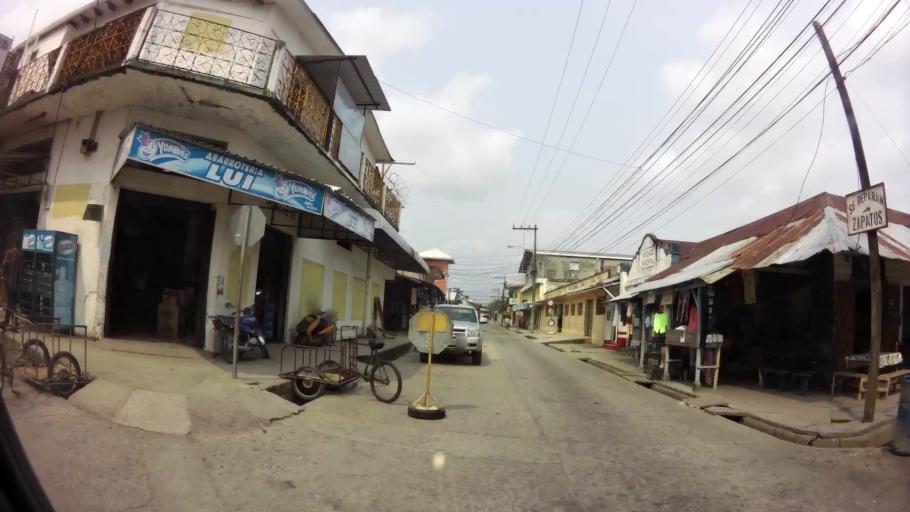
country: HN
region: Atlantida
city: Tela
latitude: 15.7836
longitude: -87.4517
